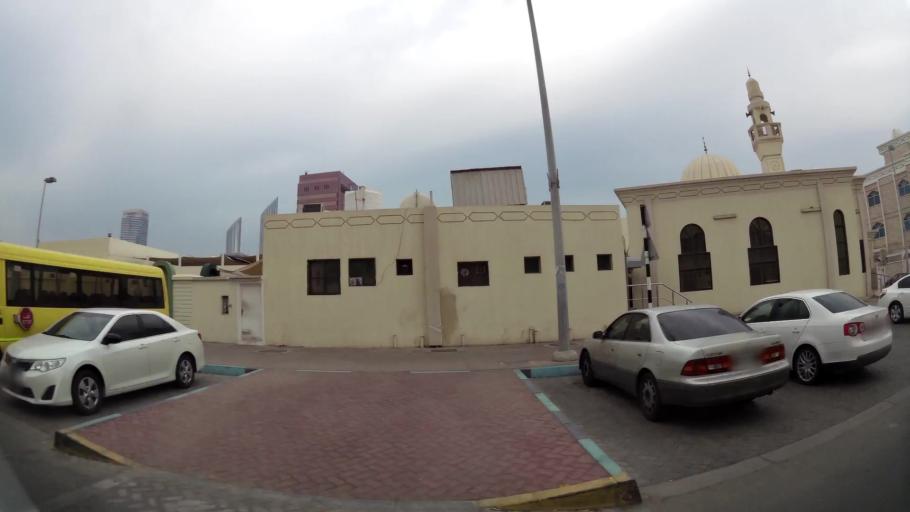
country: AE
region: Abu Dhabi
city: Abu Dhabi
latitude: 24.4815
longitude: 54.3698
